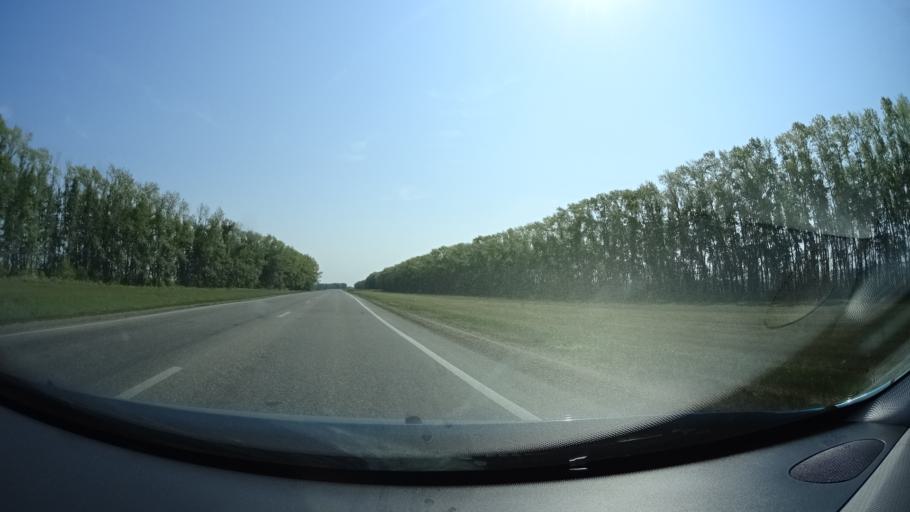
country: RU
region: Bashkortostan
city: Karmaskaly
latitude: 54.3913
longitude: 56.1211
